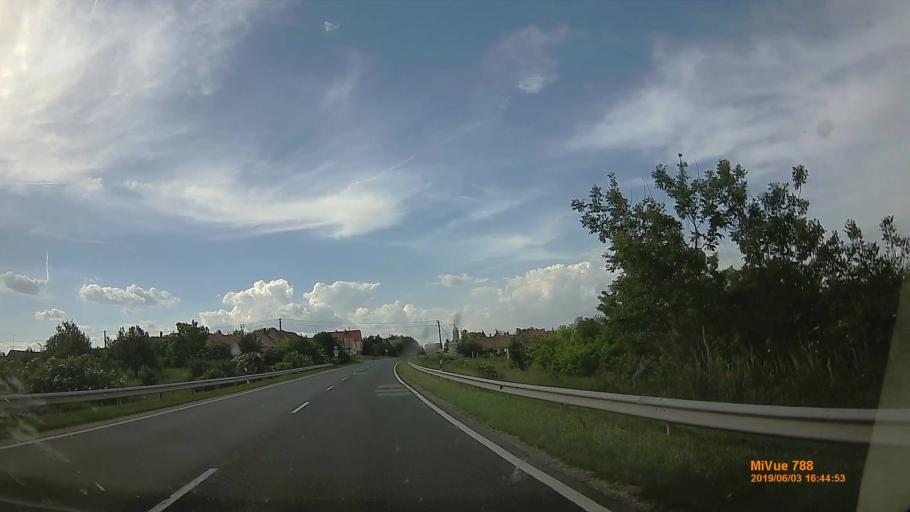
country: HU
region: Tolna
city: Simontornya
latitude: 46.7703
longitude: 18.5177
